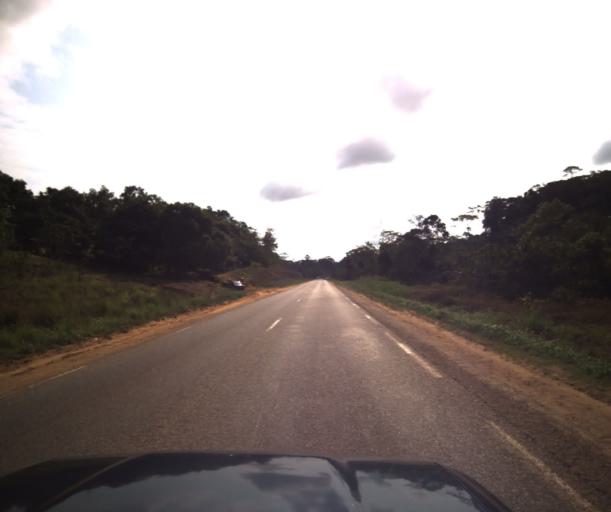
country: CM
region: Littoral
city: Dizangue
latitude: 3.9503
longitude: 10.0093
